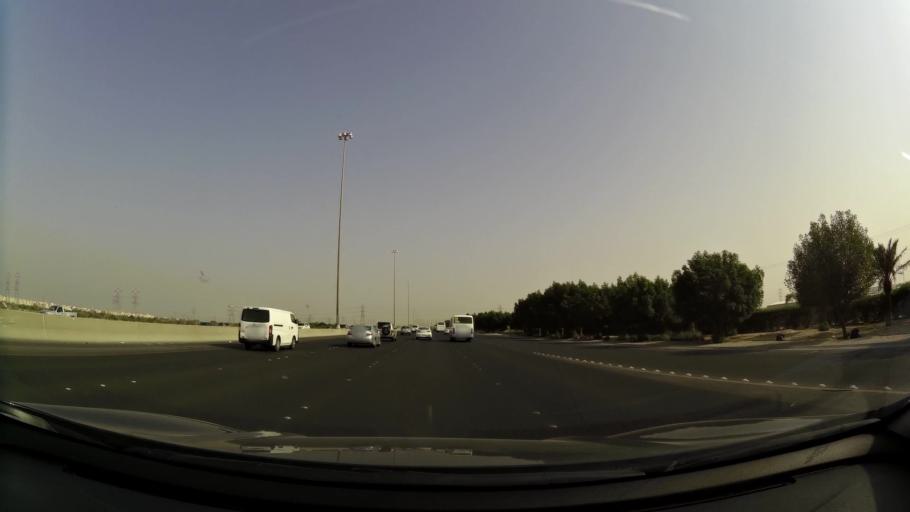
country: KW
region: Muhafazat al Jahra'
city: Al Jahra'
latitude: 29.3211
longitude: 47.7561
